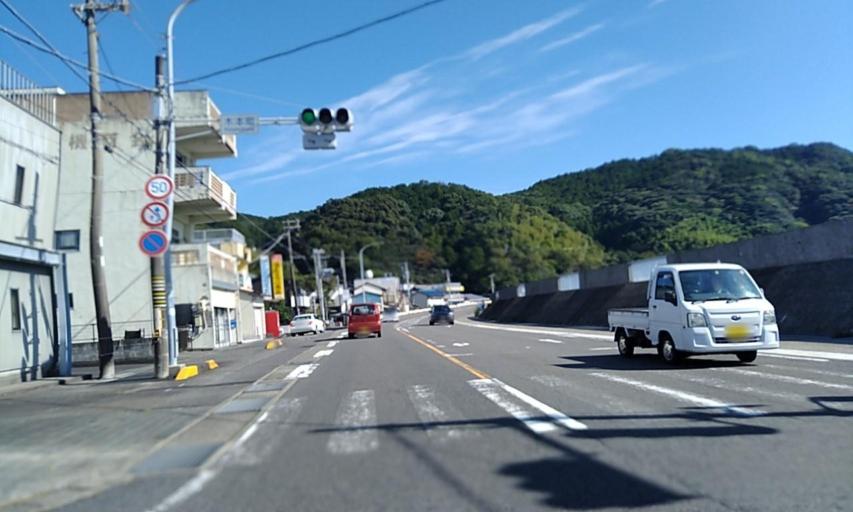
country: JP
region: Wakayama
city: Shingu
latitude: 33.8908
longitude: 136.1056
